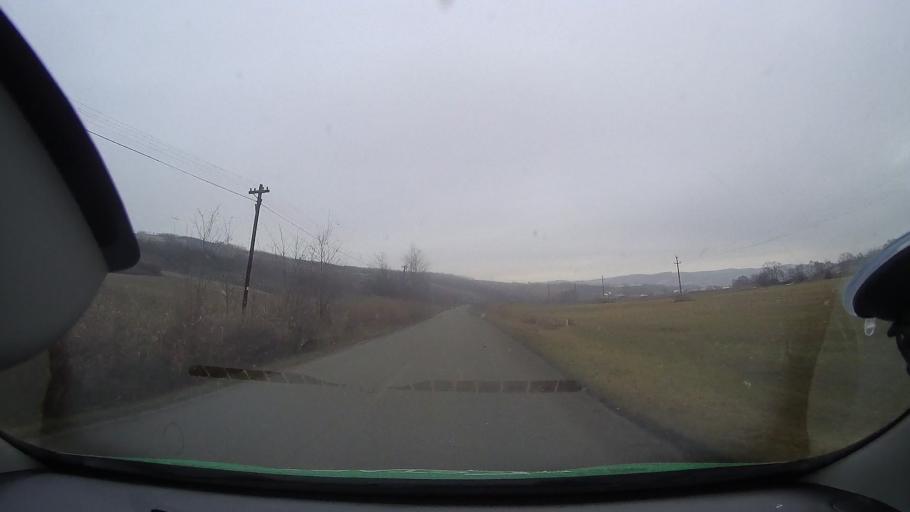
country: RO
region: Alba
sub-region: Comuna Farau
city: Farau
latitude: 46.3365
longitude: 23.9830
